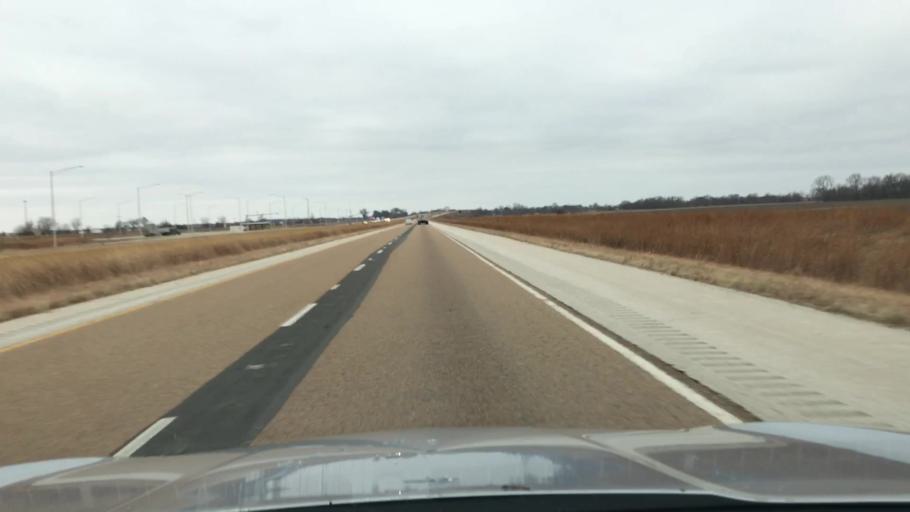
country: US
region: Illinois
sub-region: Montgomery County
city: Litchfield
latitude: 39.2310
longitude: -89.6429
